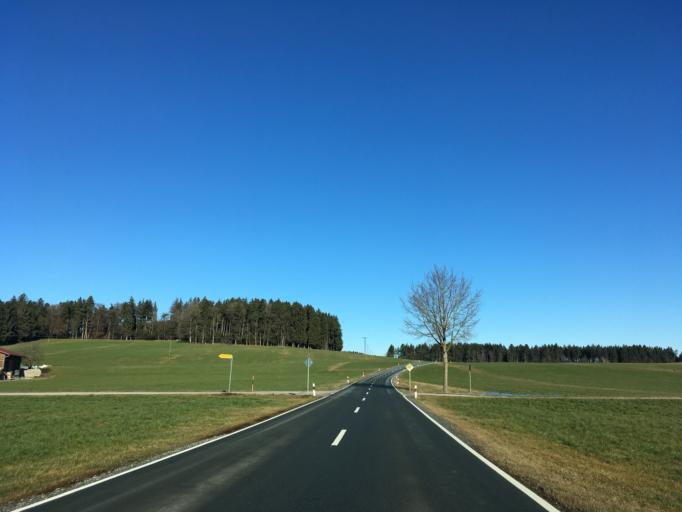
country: DE
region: Bavaria
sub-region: Upper Bavaria
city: Hoslwang
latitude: 47.9517
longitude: 12.3541
